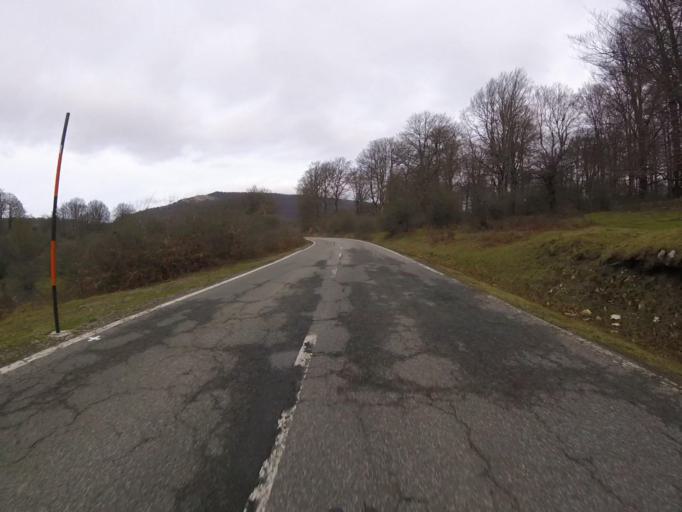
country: ES
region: Navarre
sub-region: Provincia de Navarra
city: Olazagutia
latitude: 42.8472
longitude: -2.1767
